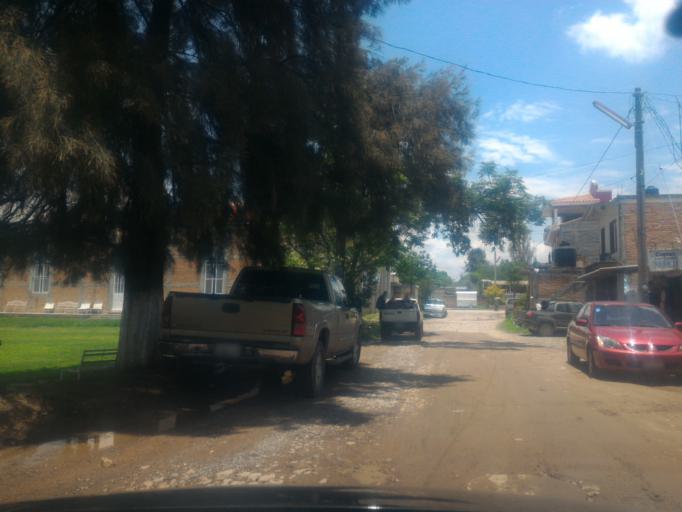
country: MX
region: Guanajuato
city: Ciudad Manuel Doblado
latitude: 20.7965
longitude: -101.9980
